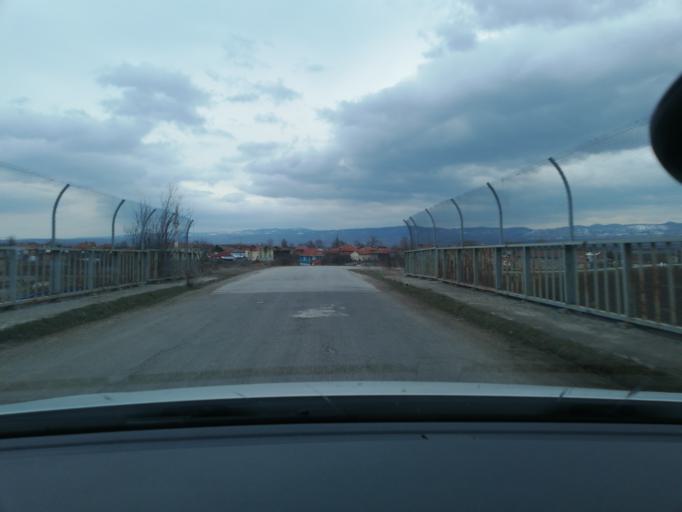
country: TR
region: Bolu
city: Gerede
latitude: 40.7564
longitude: 32.2013
